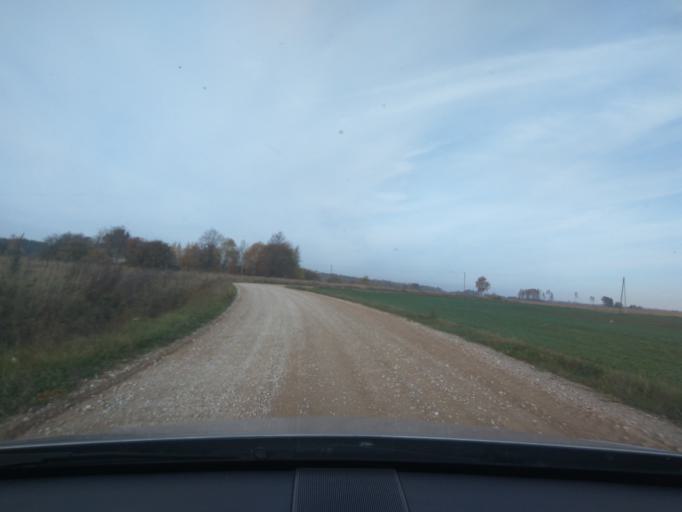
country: LV
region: Aizpute
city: Aizpute
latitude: 56.8554
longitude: 21.6672
